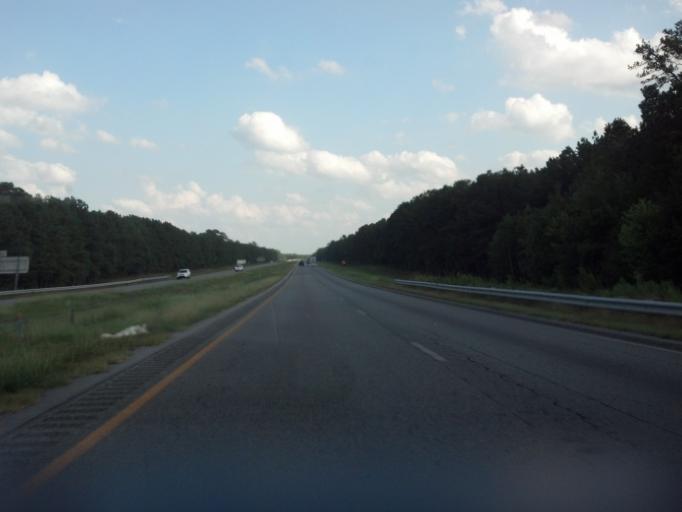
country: US
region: North Carolina
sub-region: Edgecombe County
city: Tarboro
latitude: 35.9149
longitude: -77.6537
